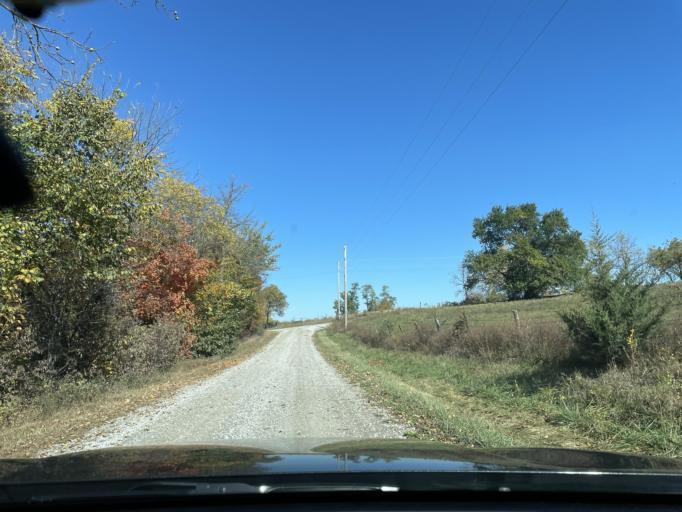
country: US
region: Missouri
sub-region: Andrew County
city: Savannah
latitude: 39.9383
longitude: -94.8803
